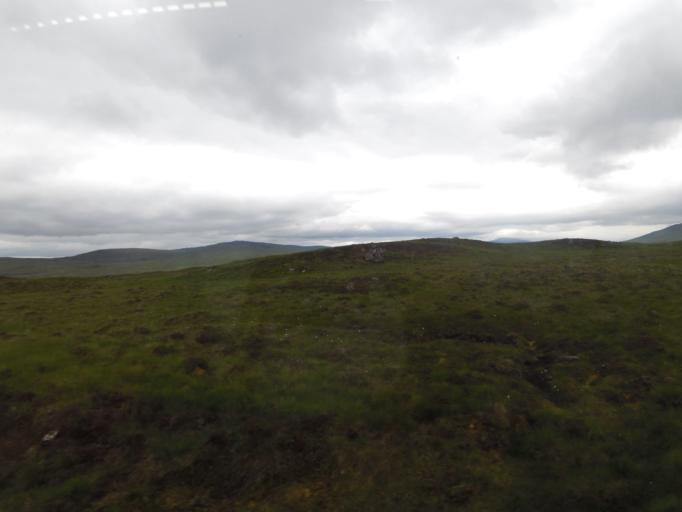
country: GB
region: Scotland
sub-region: Highland
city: Spean Bridge
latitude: 56.7250
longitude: -4.6359
